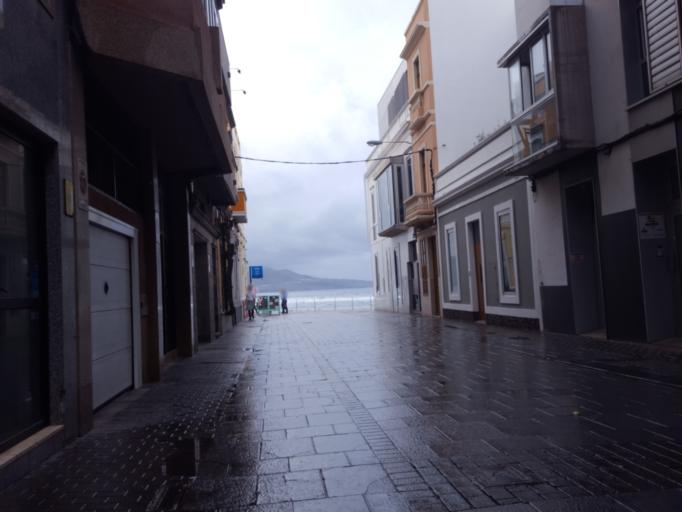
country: ES
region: Canary Islands
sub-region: Provincia de Las Palmas
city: Las Palmas de Gran Canaria
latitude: 28.1405
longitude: -15.4352
